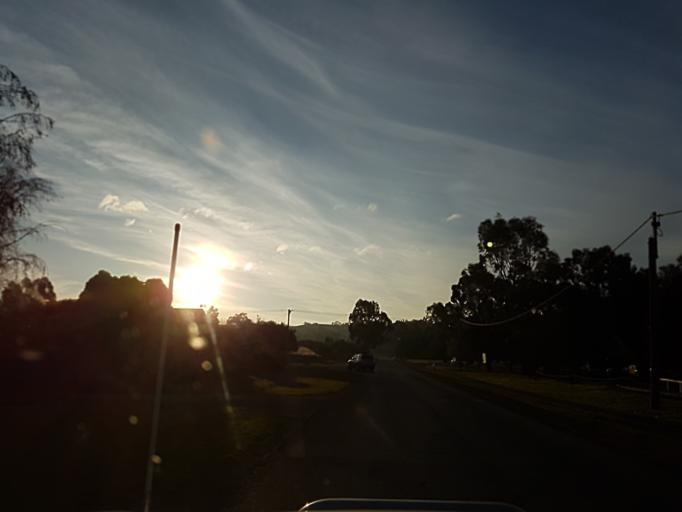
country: AU
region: Victoria
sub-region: Murrindindi
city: Alexandra
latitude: -37.1854
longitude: 145.7140
